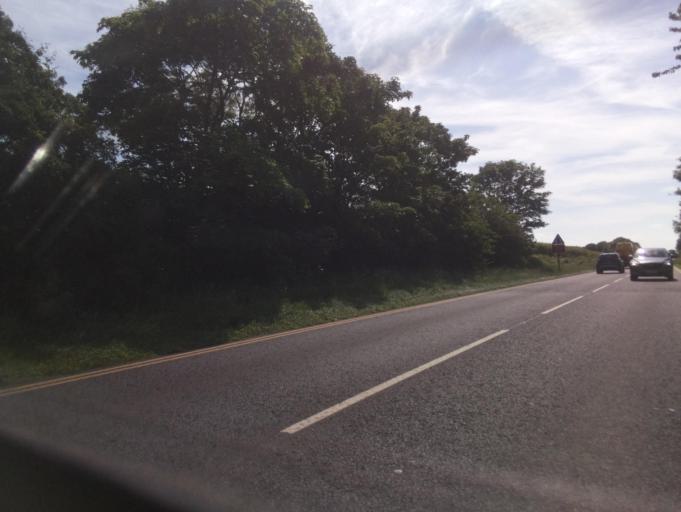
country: GB
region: England
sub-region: Lincolnshire
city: Burton
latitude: 53.3227
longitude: -0.5349
